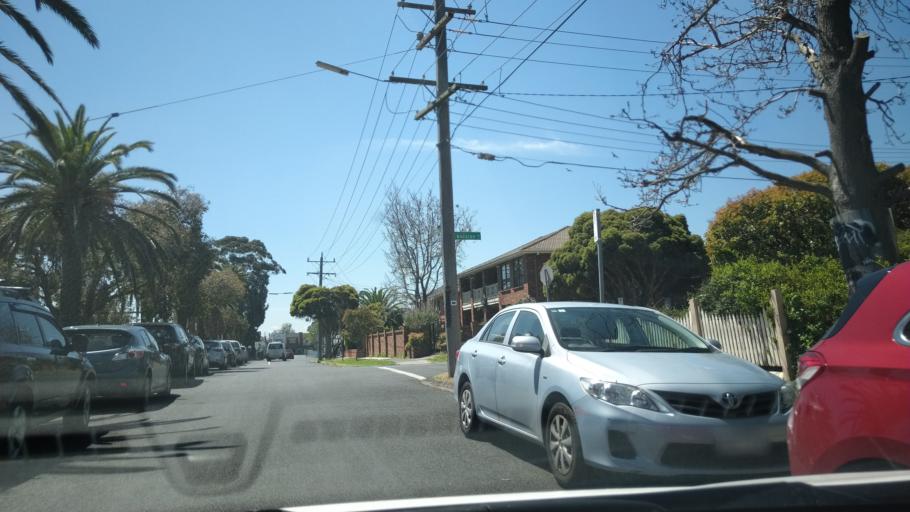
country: AU
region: Victoria
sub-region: Glen Eira
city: Glen Huntly
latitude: -37.8919
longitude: 145.0420
